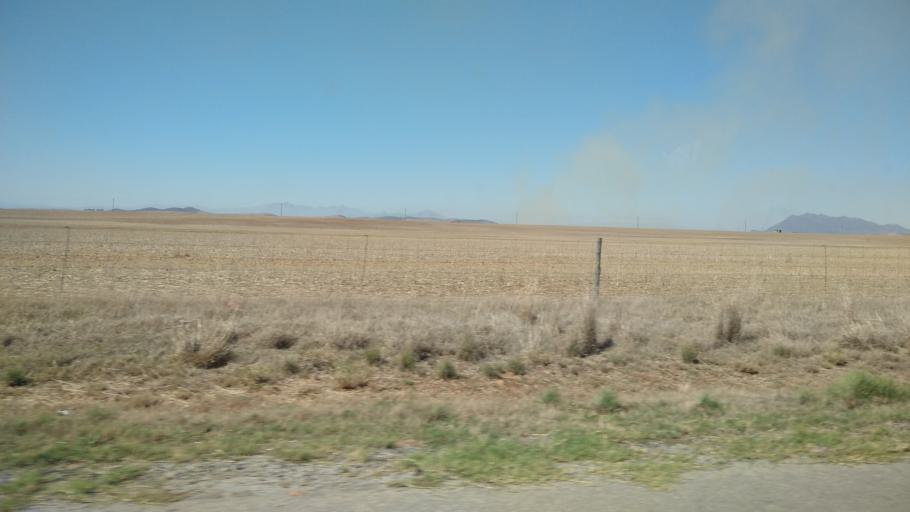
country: ZA
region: Western Cape
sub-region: West Coast District Municipality
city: Moorreesburg
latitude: -33.2949
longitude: 18.6110
